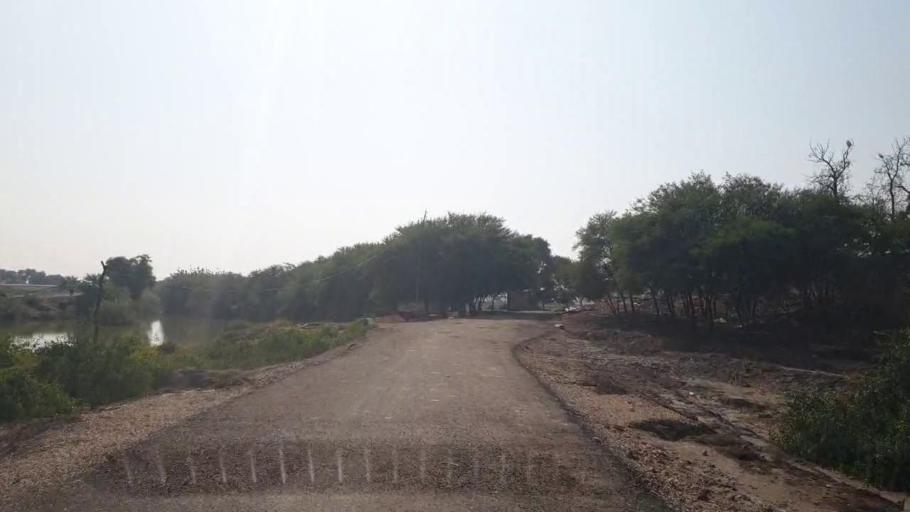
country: PK
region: Sindh
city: Sehwan
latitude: 26.4307
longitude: 67.7565
